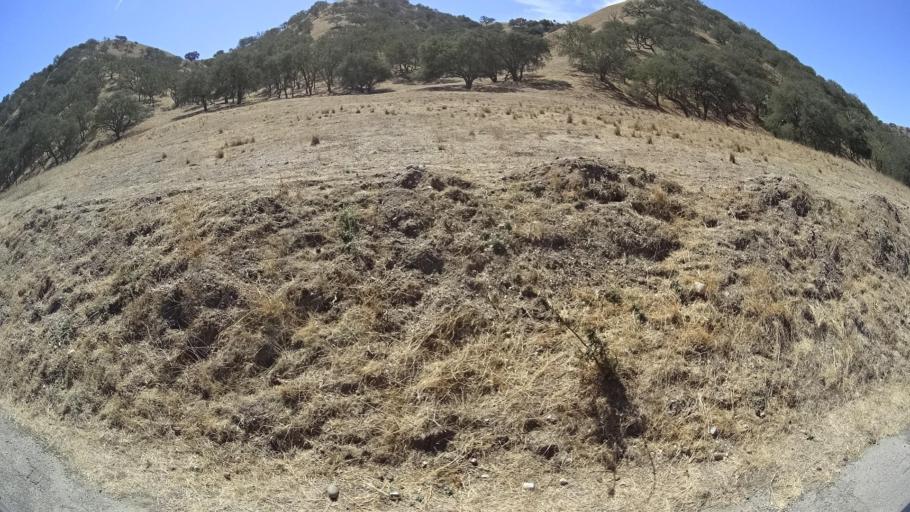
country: US
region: California
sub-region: San Luis Obispo County
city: San Miguel
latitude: 35.9443
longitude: -120.7972
